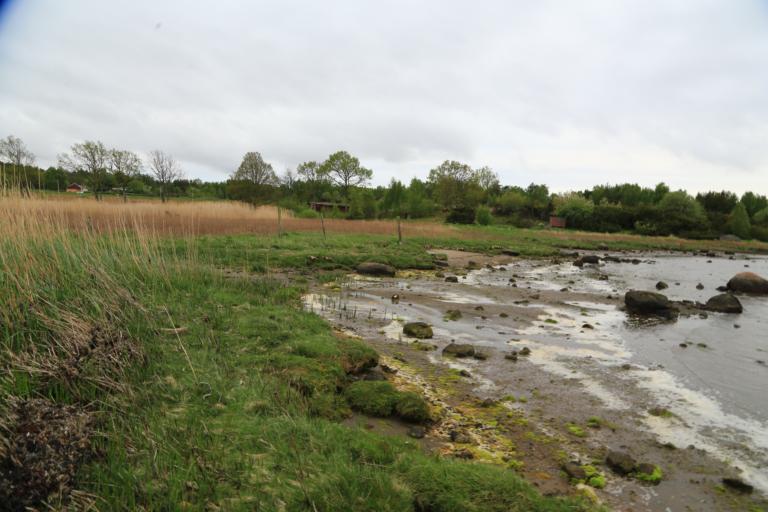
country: SE
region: Halland
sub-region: Varbergs Kommun
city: Varberg
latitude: 57.1527
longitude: 12.2198
